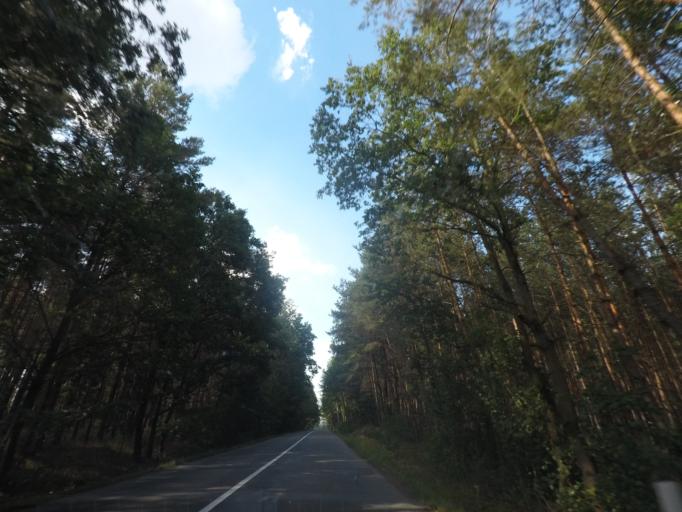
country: CZ
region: Kralovehradecky
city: Trebechovice pod Orebem
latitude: 50.2206
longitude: 15.9762
